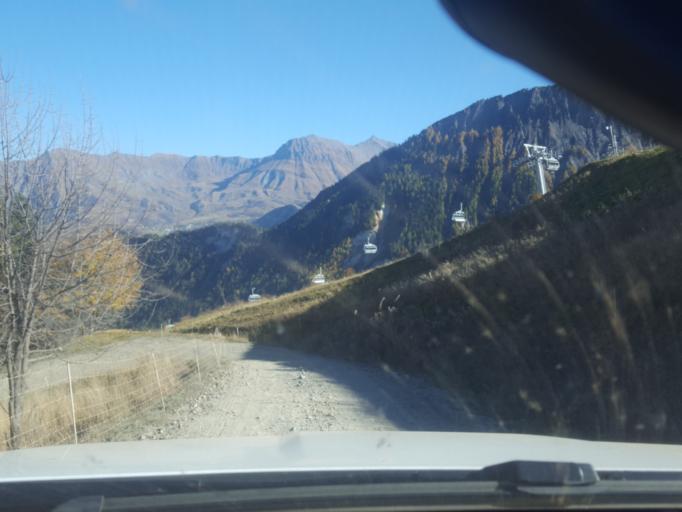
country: FR
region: Rhone-Alpes
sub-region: Departement de la Savoie
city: Saint-Jean-de-Maurienne
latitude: 45.2375
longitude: 6.2675
